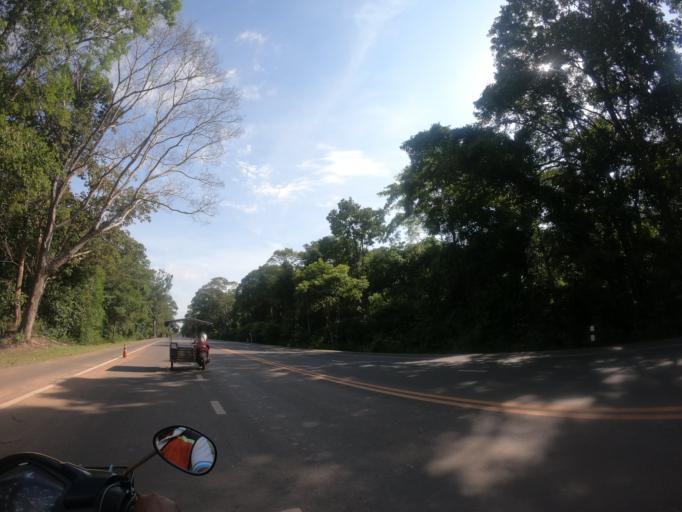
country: TH
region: Surin
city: Kap Choeng
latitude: 14.4379
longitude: 103.7007
